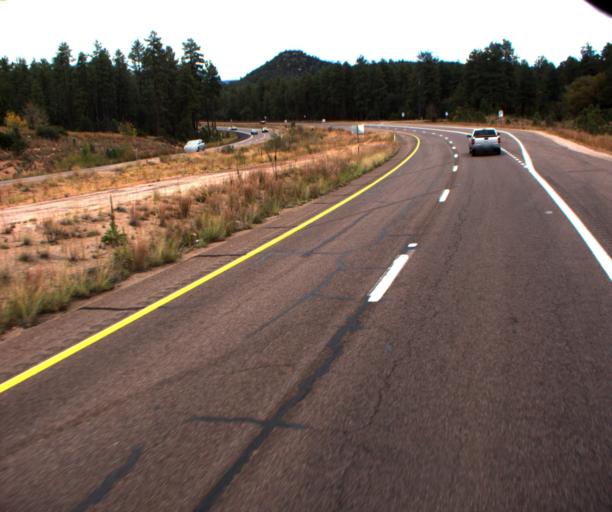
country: US
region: Arizona
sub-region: Gila County
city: Star Valley
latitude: 34.2820
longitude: -111.1452
